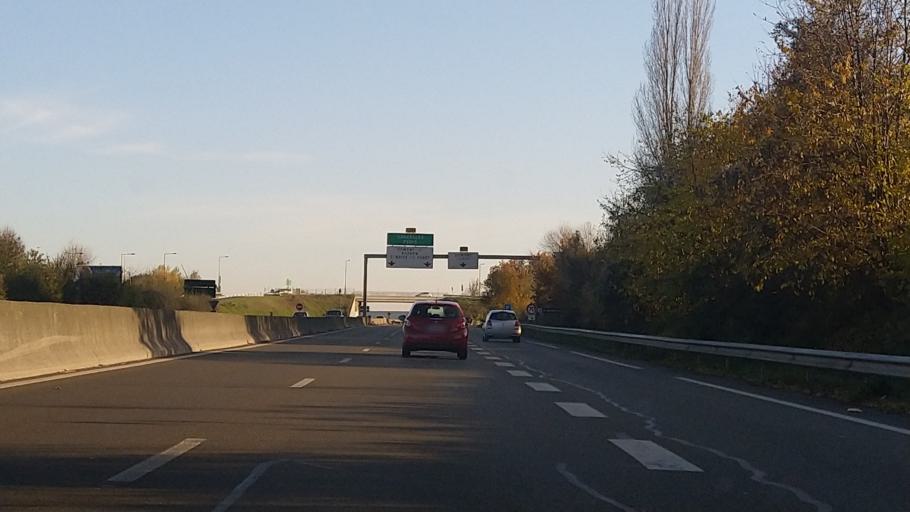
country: FR
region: Ile-de-France
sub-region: Departement du Val-d'Oise
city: Moisselles
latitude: 49.0457
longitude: 2.3349
